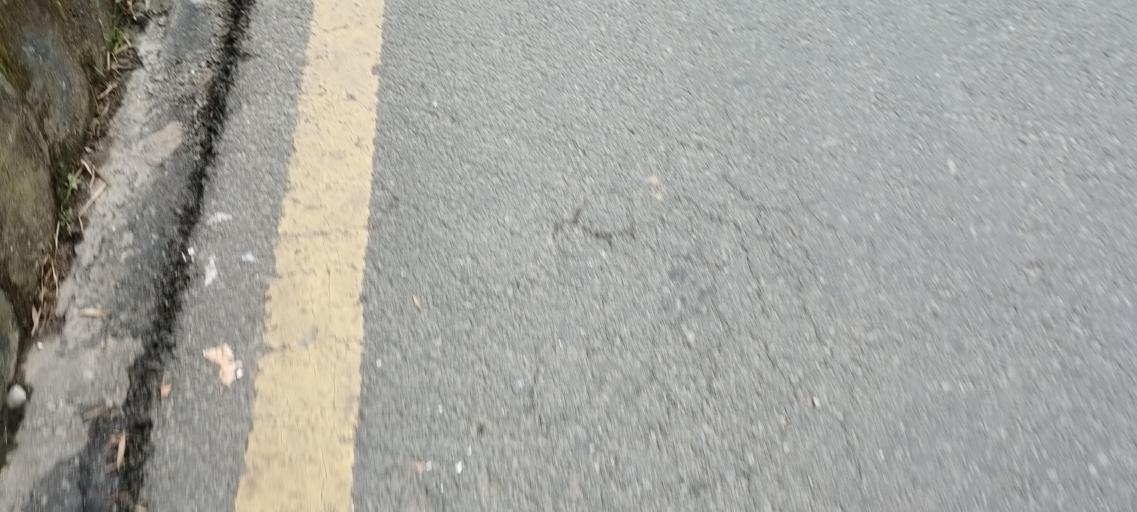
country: NP
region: Central Region
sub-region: Bagmati Zone
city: Kathmandu
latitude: 27.7827
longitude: 85.3640
